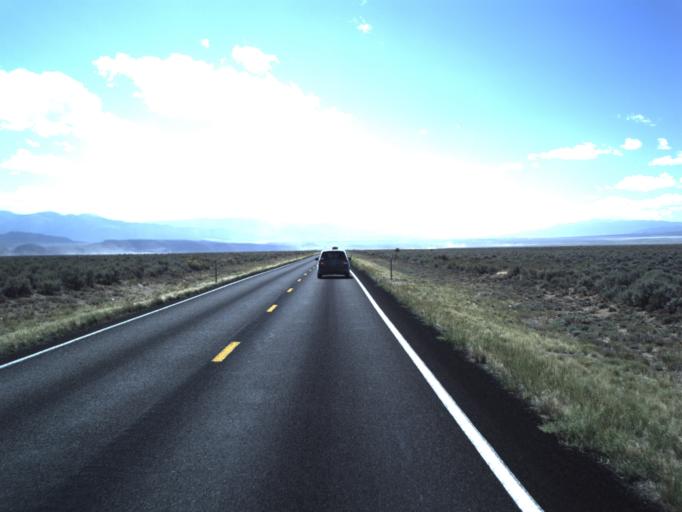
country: US
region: Utah
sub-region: Iron County
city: Enoch
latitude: 37.9918
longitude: -113.0006
